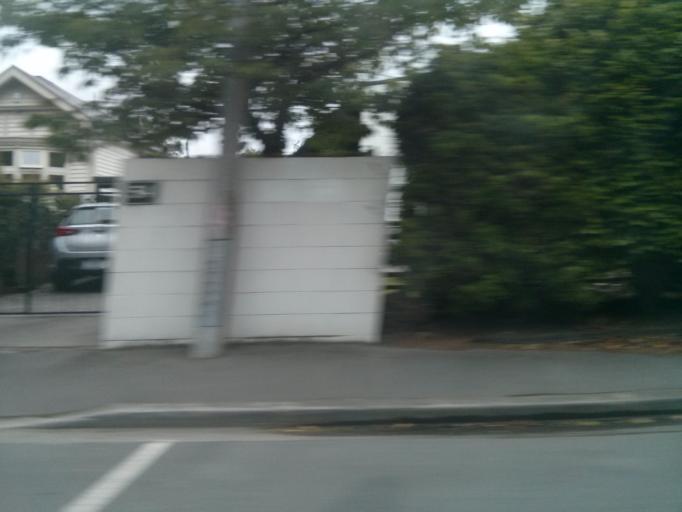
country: NZ
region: Canterbury
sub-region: Christchurch City
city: Christchurch
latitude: -43.5253
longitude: 172.6024
